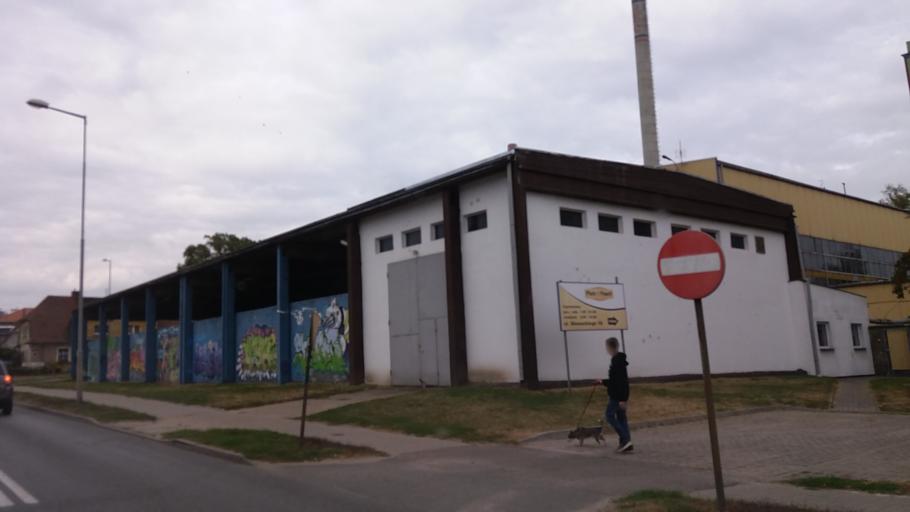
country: PL
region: Lubusz
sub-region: Powiat strzelecko-drezdenecki
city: Strzelce Krajenskie
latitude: 52.8797
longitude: 15.5252
